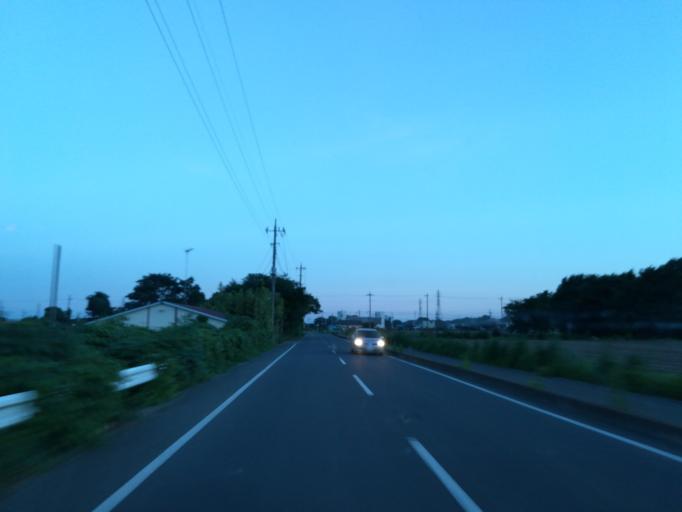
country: JP
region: Ibaraki
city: Makabe
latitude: 36.2380
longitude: 140.0550
